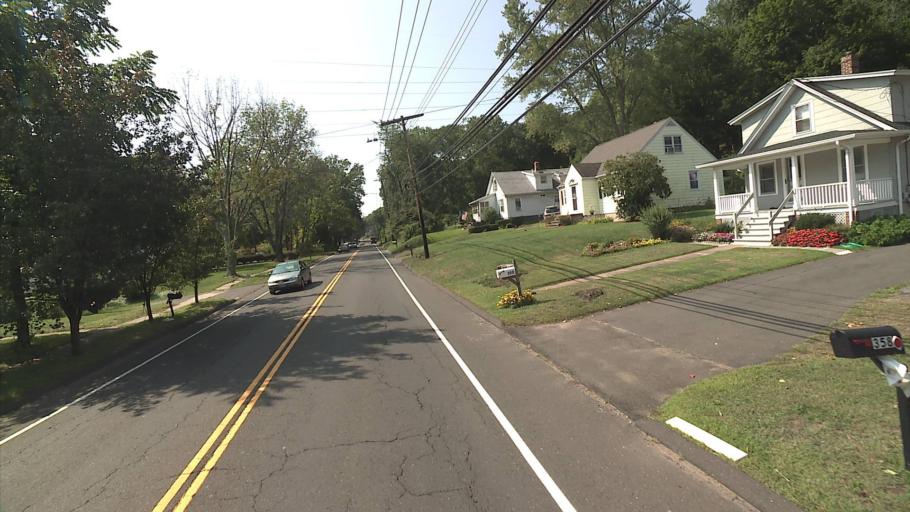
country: US
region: Connecticut
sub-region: New Haven County
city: East Haven
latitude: 41.2898
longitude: -72.8681
